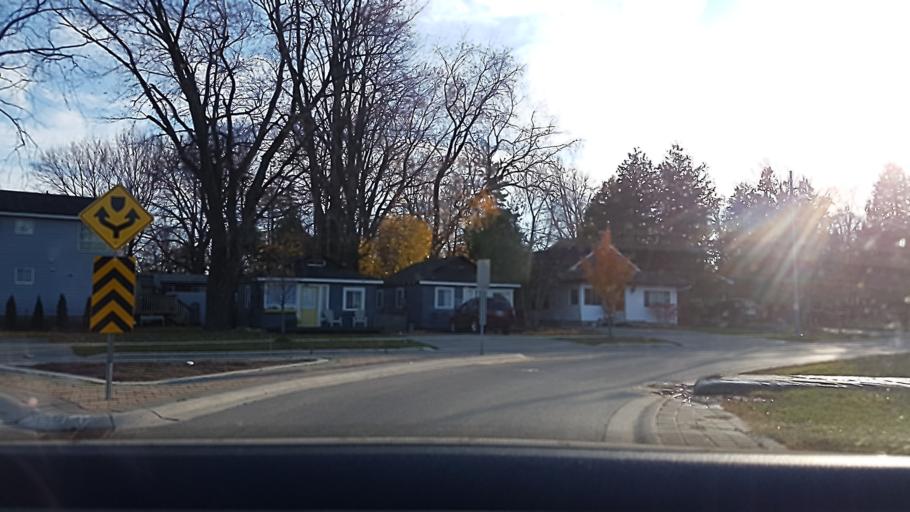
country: CA
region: Ontario
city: Keswick
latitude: 44.3182
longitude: -79.5338
